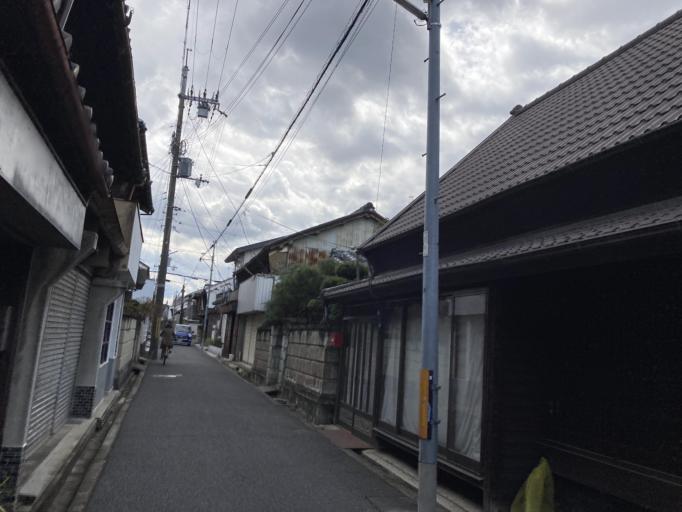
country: JP
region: Nara
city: Kashihara-shi
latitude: 34.5074
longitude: 135.7958
